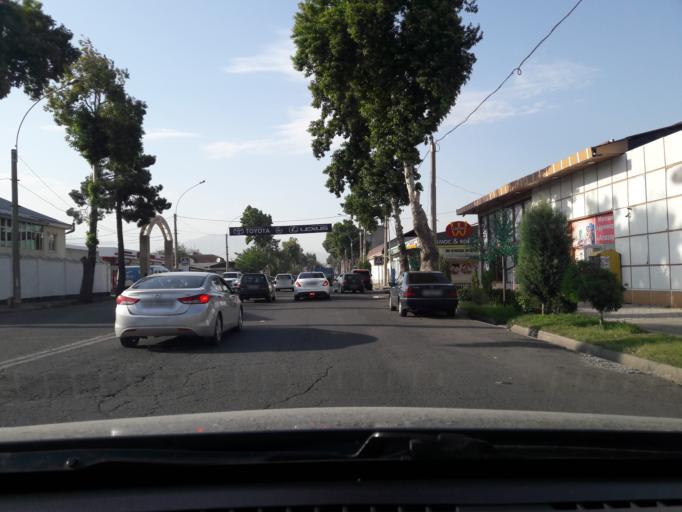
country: TJ
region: Dushanbe
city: Dushanbe
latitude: 38.5480
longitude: 68.7720
